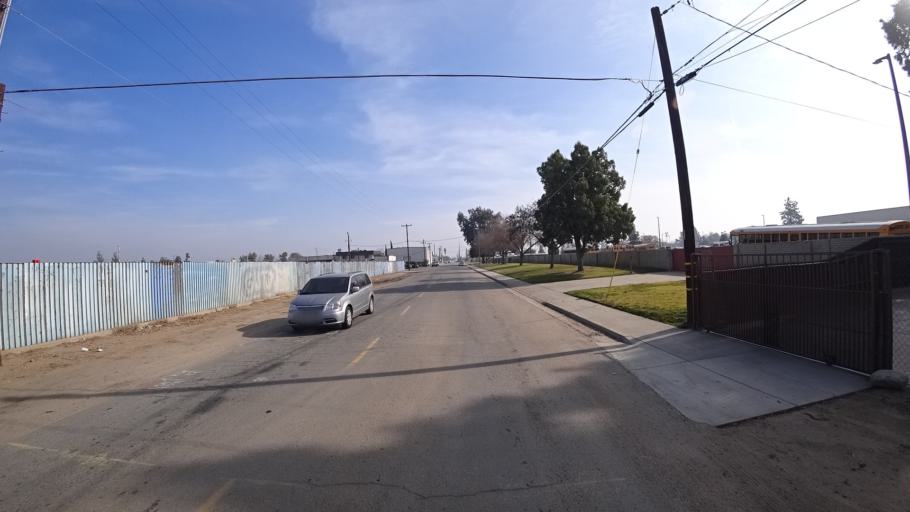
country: US
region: California
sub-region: Kern County
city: Bakersfield
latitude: 35.3503
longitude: -119.0067
